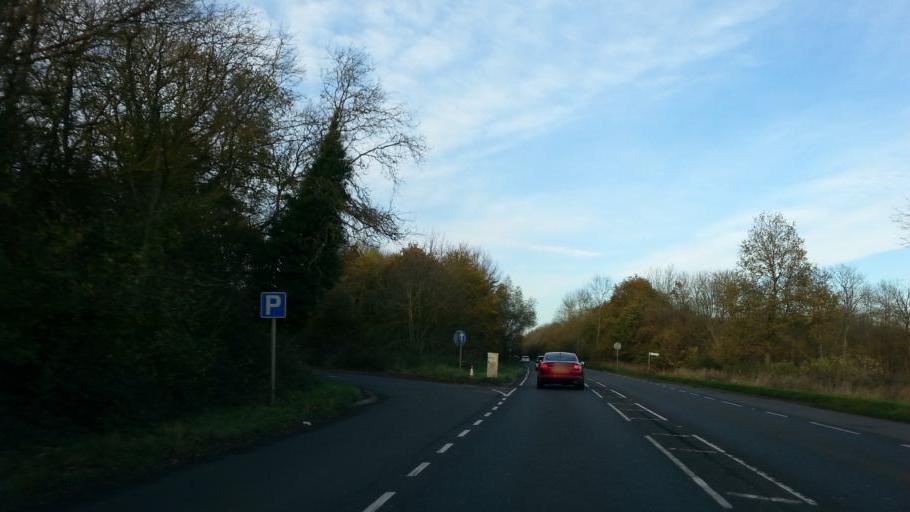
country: GB
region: England
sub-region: Northamptonshire
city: Broughton
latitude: 52.3246
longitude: -0.7932
